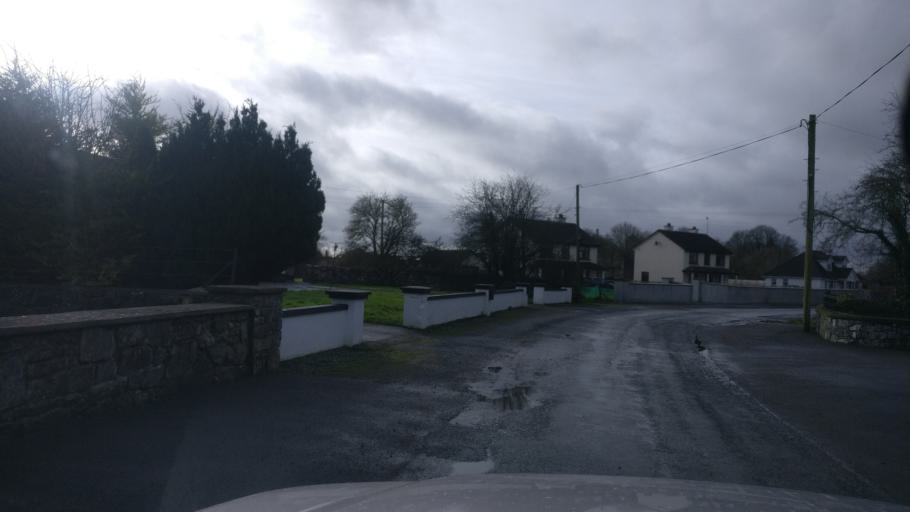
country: IE
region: Connaught
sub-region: County Galway
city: Athenry
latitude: 53.2635
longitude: -8.7938
